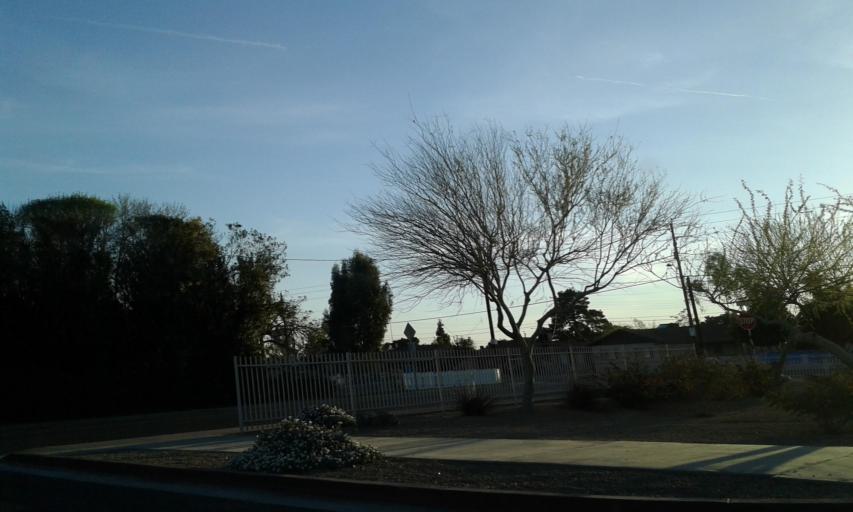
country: US
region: Arizona
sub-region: Maricopa County
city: Glendale
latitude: 33.5298
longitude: -112.1077
